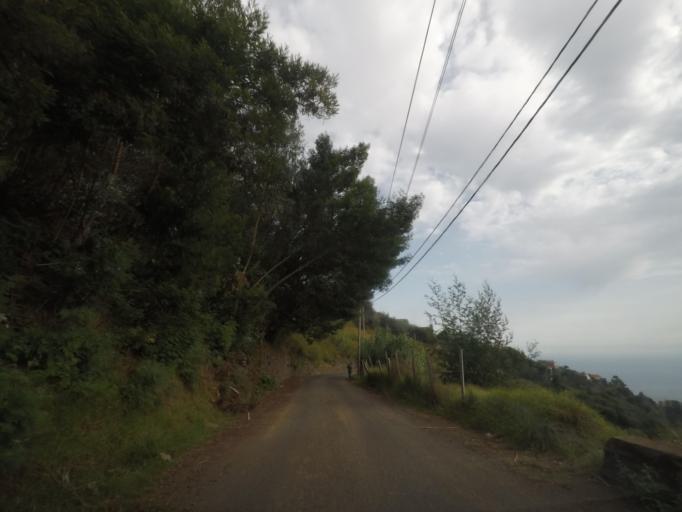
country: PT
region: Madeira
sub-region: Calheta
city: Arco da Calheta
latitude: 32.7365
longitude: -17.1537
